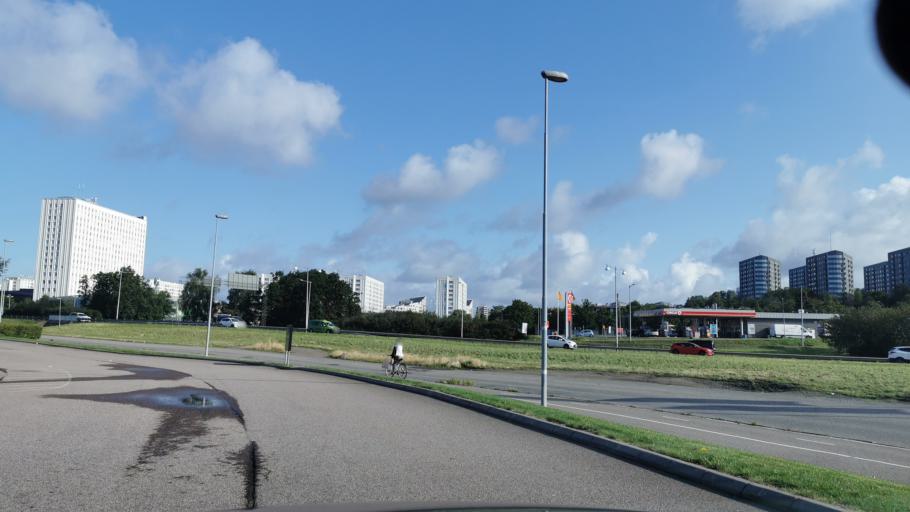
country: SE
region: Vaestra Goetaland
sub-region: Goteborg
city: Majorna
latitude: 57.6475
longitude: 11.9154
